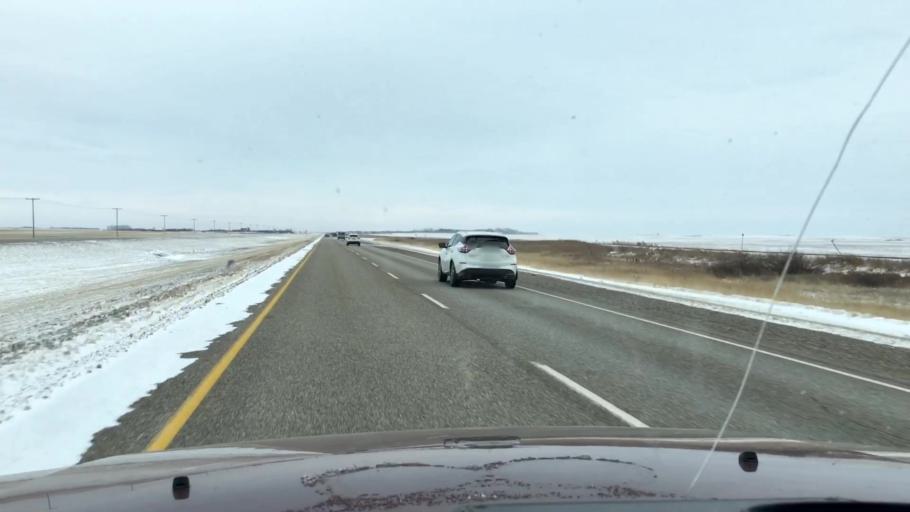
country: CA
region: Saskatchewan
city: Moose Jaw
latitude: 50.9931
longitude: -105.7558
